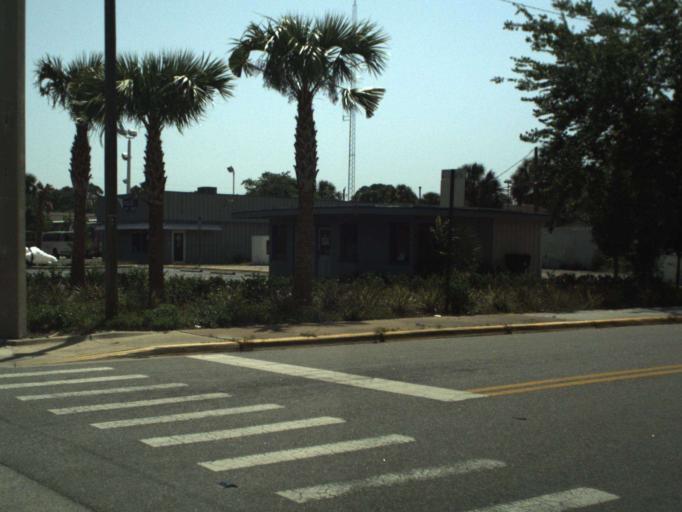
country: US
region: Florida
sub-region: Volusia County
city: Daytona Beach
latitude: 29.2050
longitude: -81.0359
